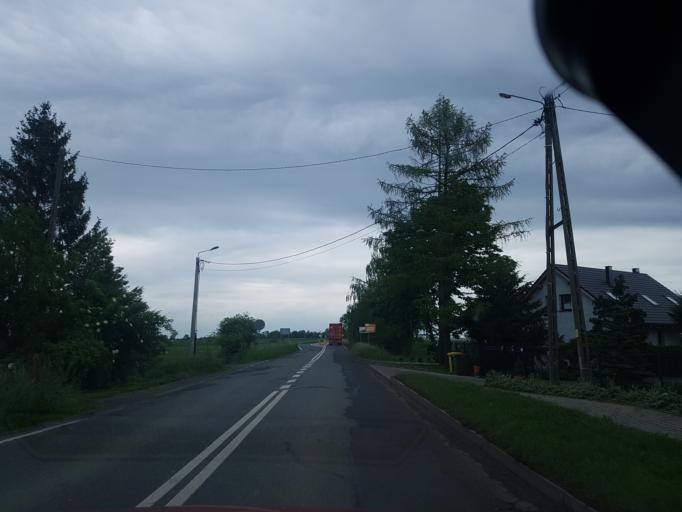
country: PL
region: Lower Silesian Voivodeship
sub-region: Powiat wroclawski
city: Zorawina
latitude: 50.9289
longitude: 17.0436
